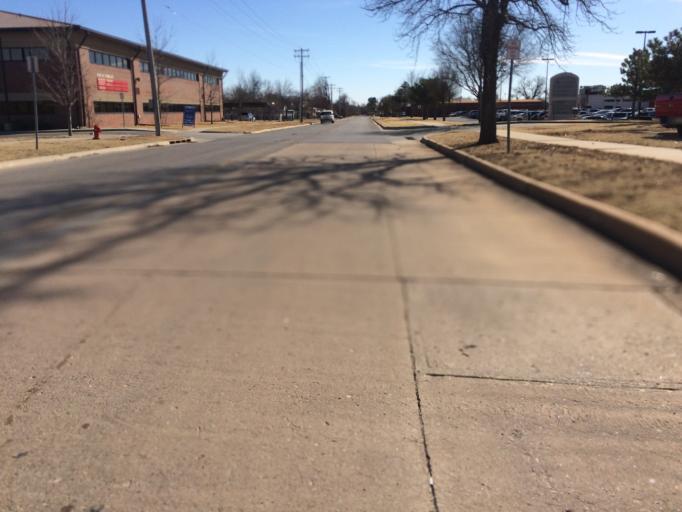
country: US
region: Oklahoma
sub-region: Cleveland County
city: Norman
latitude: 35.2323
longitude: -97.4376
